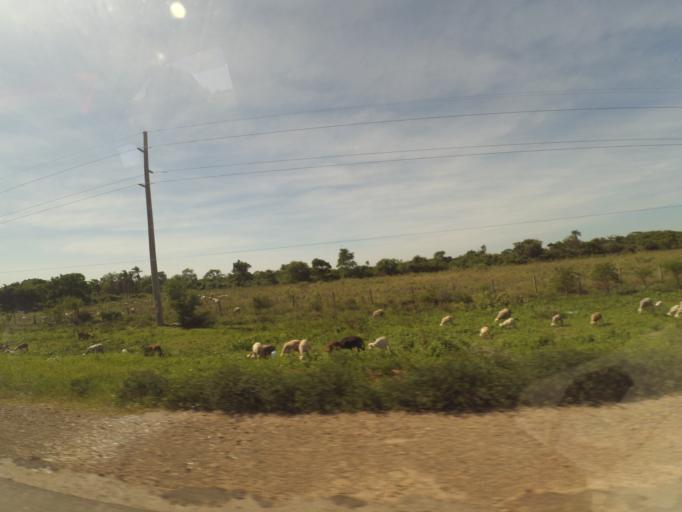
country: BO
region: Santa Cruz
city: San Julian
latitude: -17.7434
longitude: -62.9509
